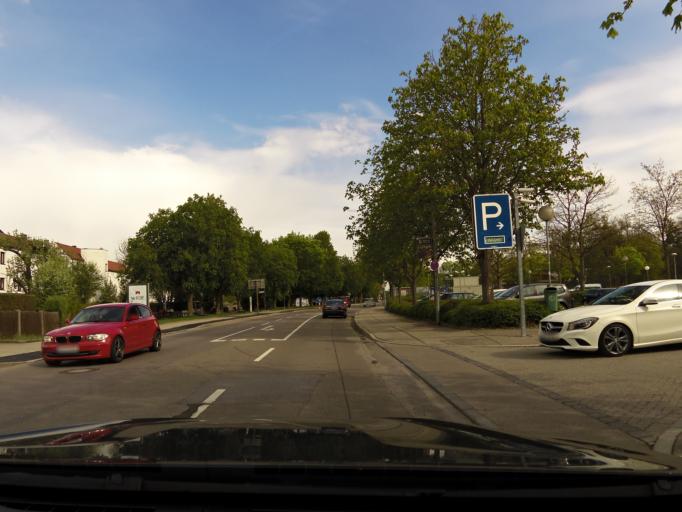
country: DE
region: Bavaria
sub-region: Upper Bavaria
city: Ingolstadt
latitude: 48.7610
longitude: 11.4212
